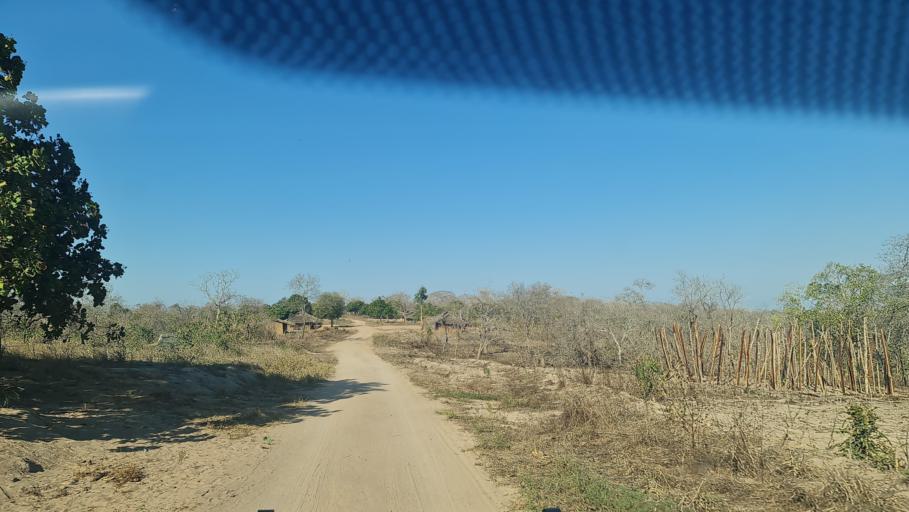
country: MZ
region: Nampula
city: Nacala
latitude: -13.9438
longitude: 40.4815
